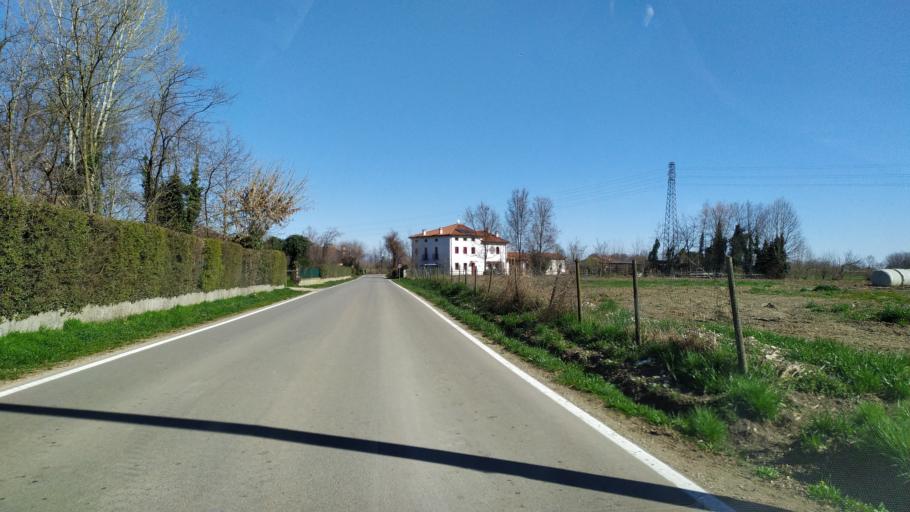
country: IT
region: Veneto
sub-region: Provincia di Vicenza
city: Sandrigo
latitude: 45.6349
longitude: 11.5936
